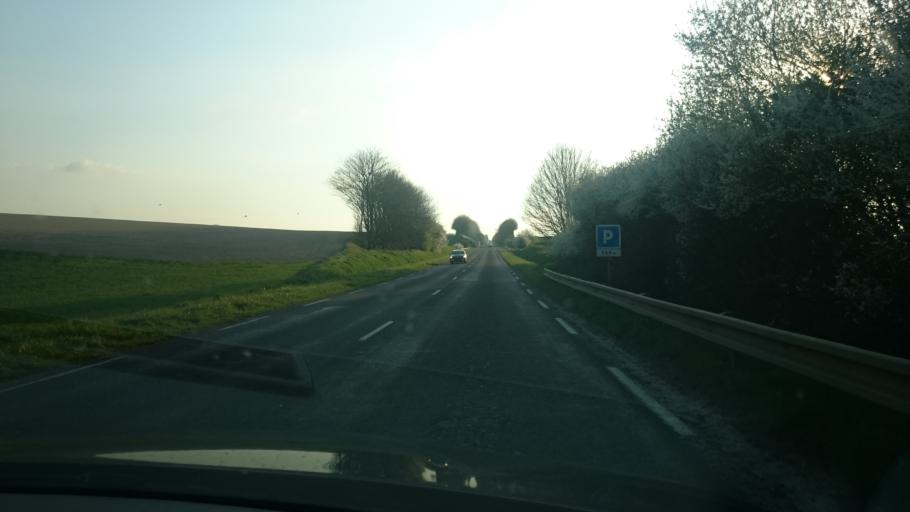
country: FR
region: Picardie
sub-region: Departement de l'Aisne
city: Guise
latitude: 49.8791
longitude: 3.5928
